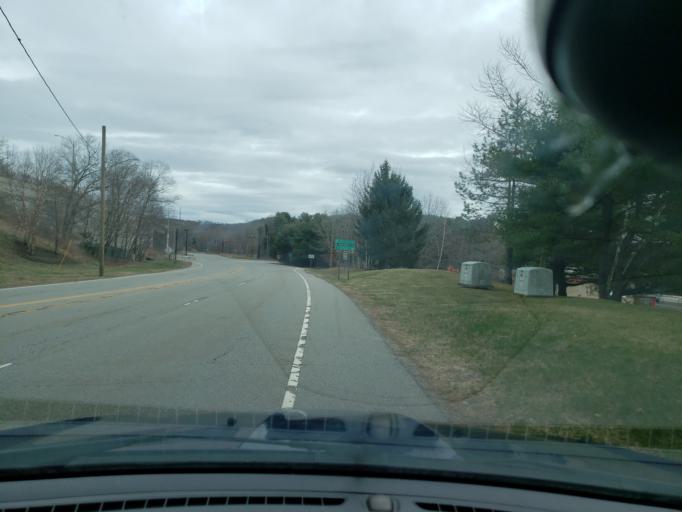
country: US
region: Connecticut
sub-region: New London County
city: Preston City
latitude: 41.4711
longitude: -71.9532
